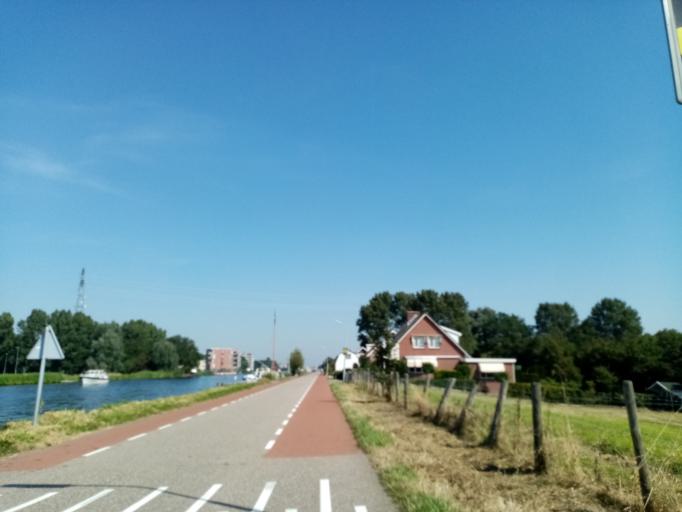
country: NL
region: South Holland
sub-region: Gemeente Lisse
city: Lisse
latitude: 52.2380
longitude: 4.5646
